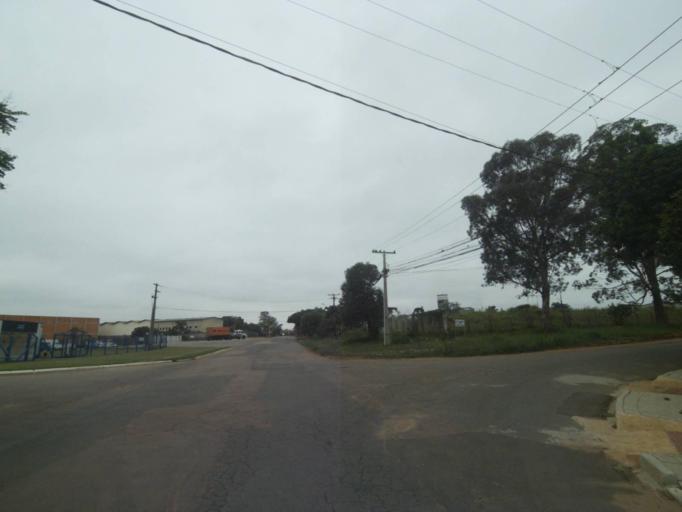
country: BR
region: Parana
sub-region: Araucaria
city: Araucaria
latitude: -25.5439
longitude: -49.3323
